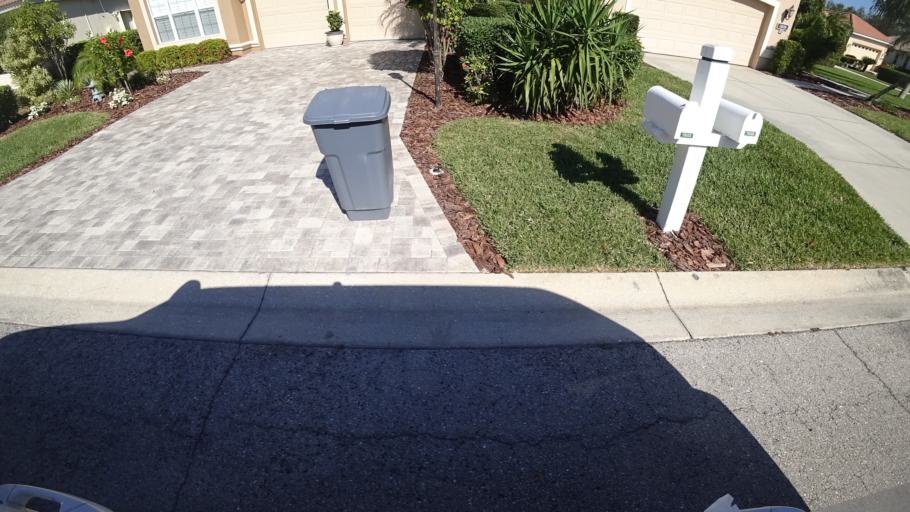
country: US
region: Florida
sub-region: Sarasota County
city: Desoto Lakes
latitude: 27.4243
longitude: -82.4609
